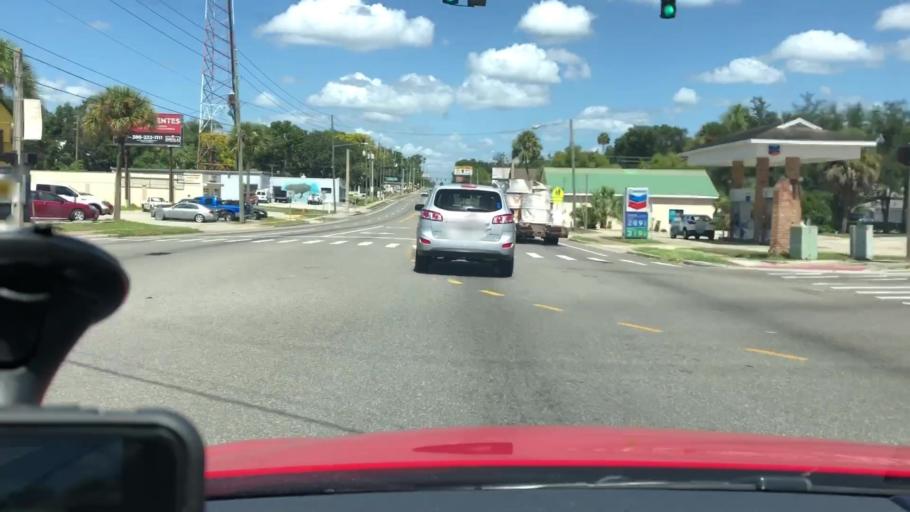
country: US
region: Florida
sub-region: Volusia County
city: Orange City
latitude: 28.9487
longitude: -81.2988
